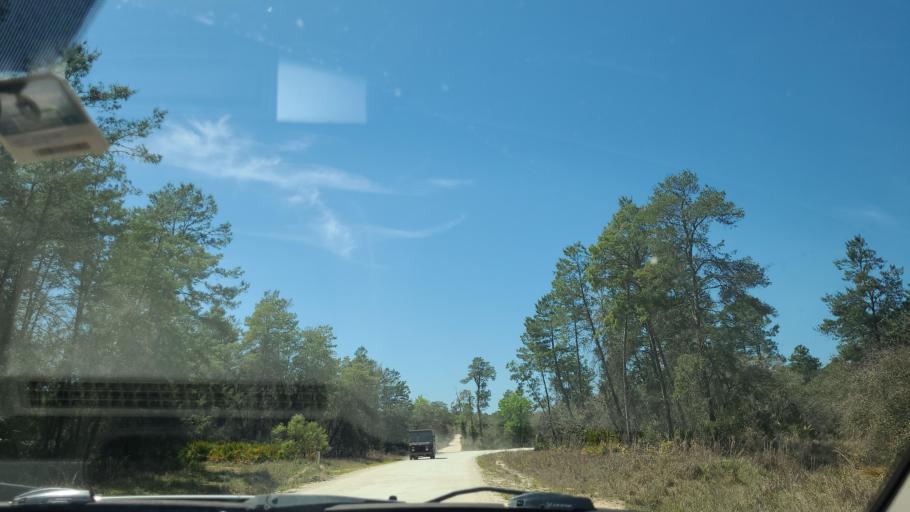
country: US
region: Florida
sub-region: Putnam County
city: Interlachen
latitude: 29.4328
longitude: -81.7542
